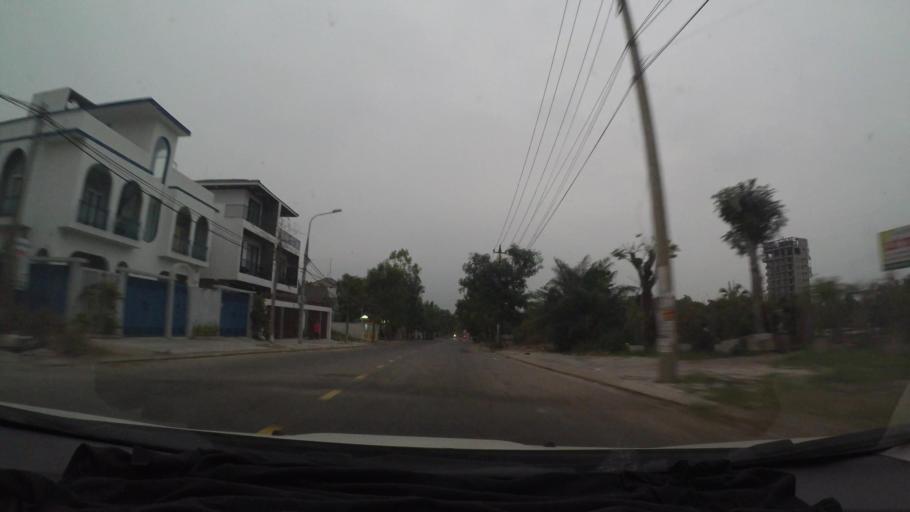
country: VN
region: Da Nang
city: Ngu Hanh Son
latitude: 16.0361
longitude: 108.2416
